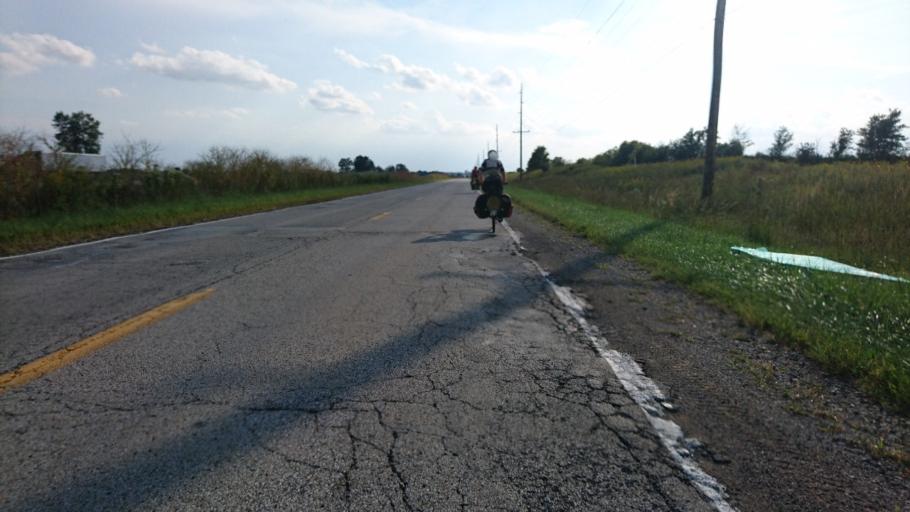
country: US
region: Illinois
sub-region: Logan County
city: Atlanta
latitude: 40.2958
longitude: -89.1912
